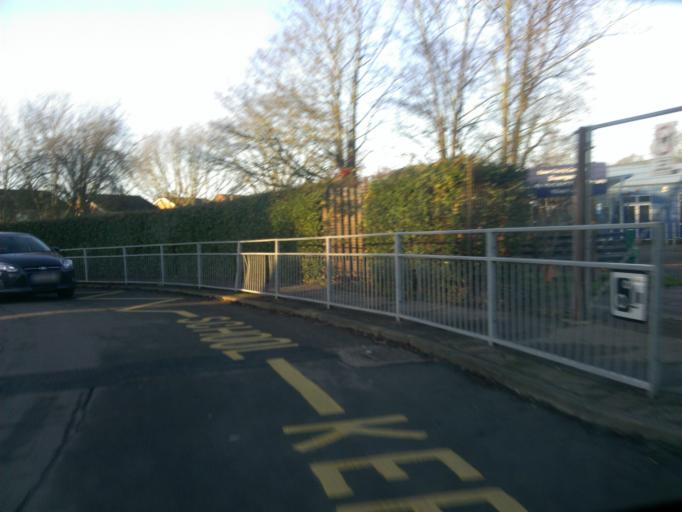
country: GB
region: England
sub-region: Essex
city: Wivenhoe
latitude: 51.8680
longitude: 0.9571
